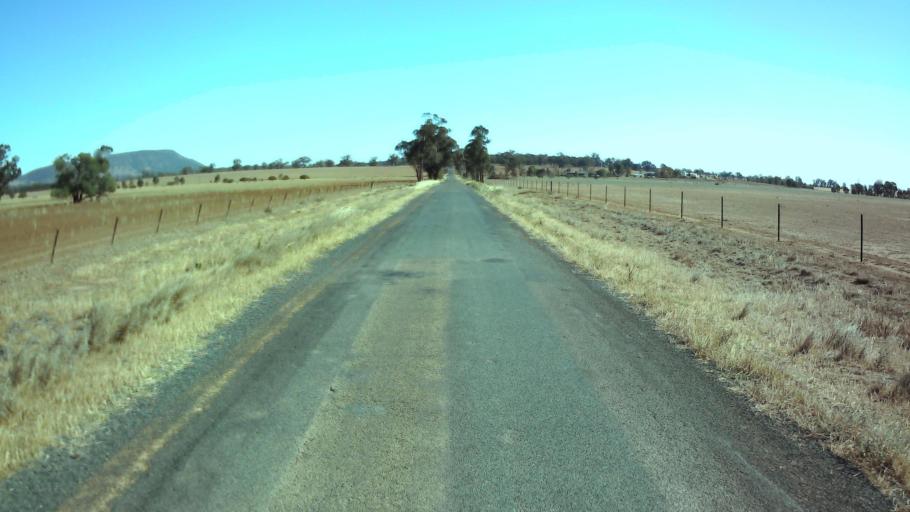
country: AU
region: New South Wales
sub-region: Weddin
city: Grenfell
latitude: -33.7978
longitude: 147.9563
